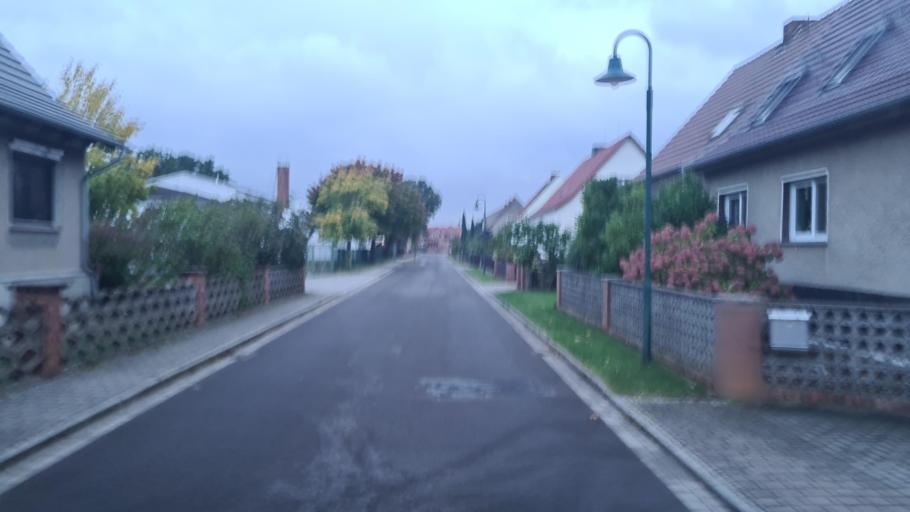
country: DE
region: Brandenburg
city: Schlepzig
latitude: 52.0286
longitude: 13.9041
